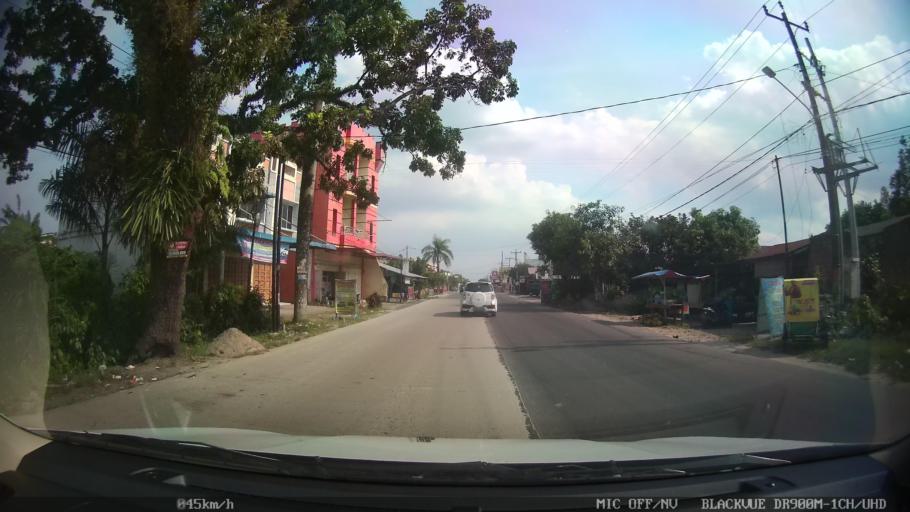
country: ID
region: North Sumatra
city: Binjai
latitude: 3.6252
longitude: 98.4952
